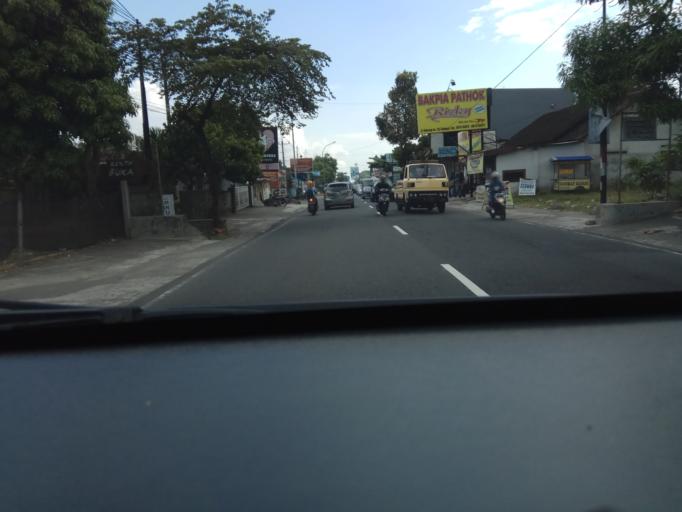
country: ID
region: Daerah Istimewa Yogyakarta
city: Melati
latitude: -7.7166
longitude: 110.4057
